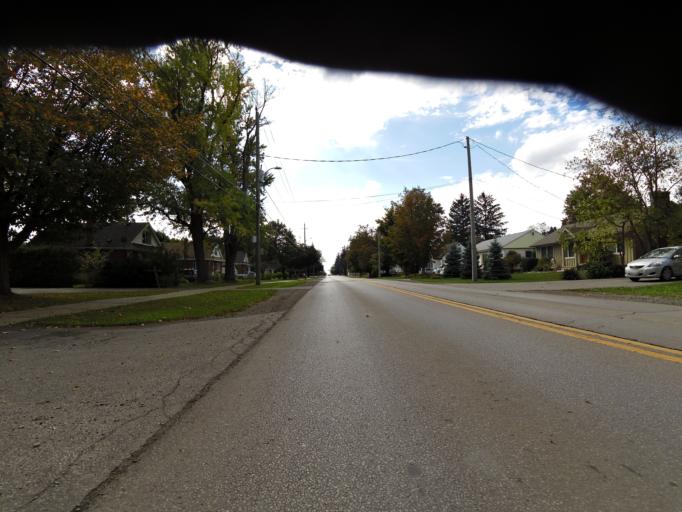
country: CA
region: Ontario
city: Burlington
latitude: 43.3428
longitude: -79.8966
